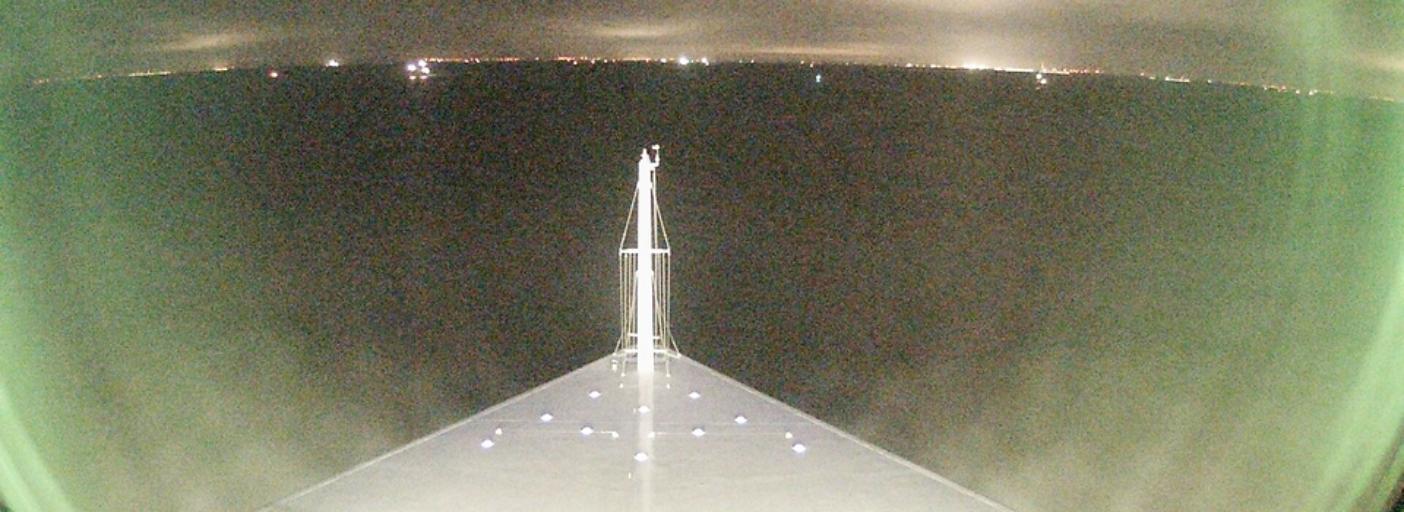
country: DE
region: Lower Saxony
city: Cuxhaven
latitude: 53.9693
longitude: 8.5278
